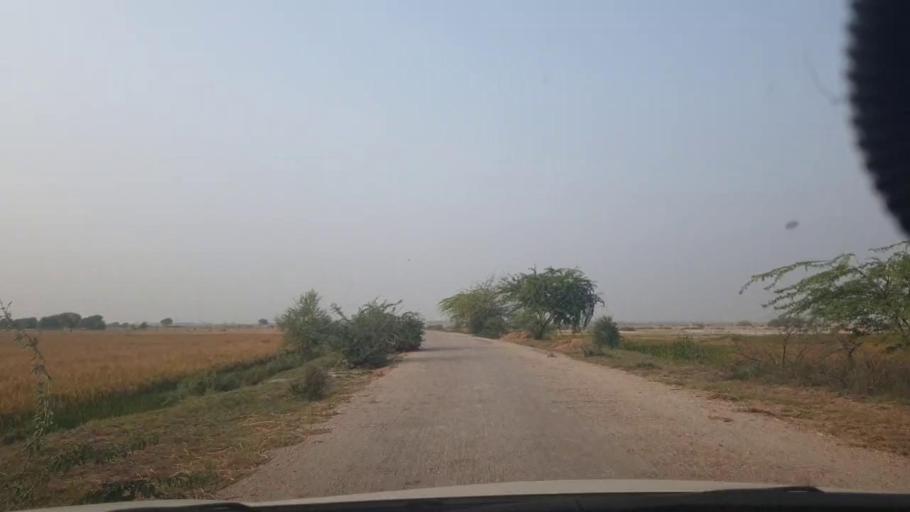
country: PK
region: Sindh
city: Bulri
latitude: 24.8115
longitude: 68.4084
